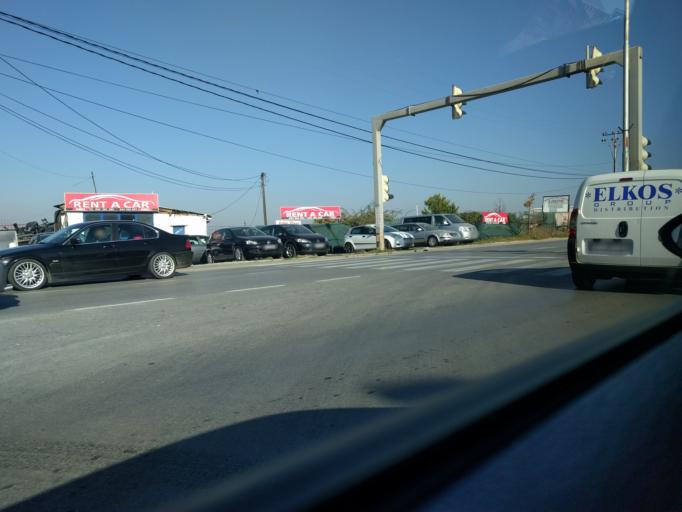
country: XK
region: Prizren
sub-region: Prizren
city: Prizren
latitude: 42.2311
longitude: 20.7563
